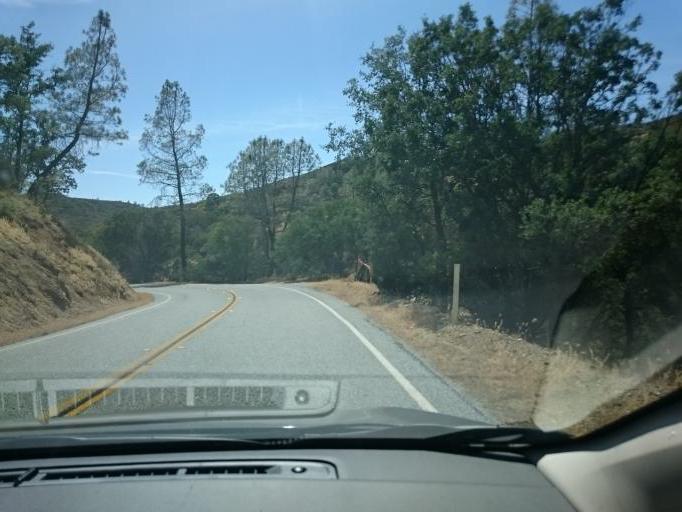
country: US
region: California
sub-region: Santa Clara County
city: Morgan Hill
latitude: 37.3879
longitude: -121.4523
